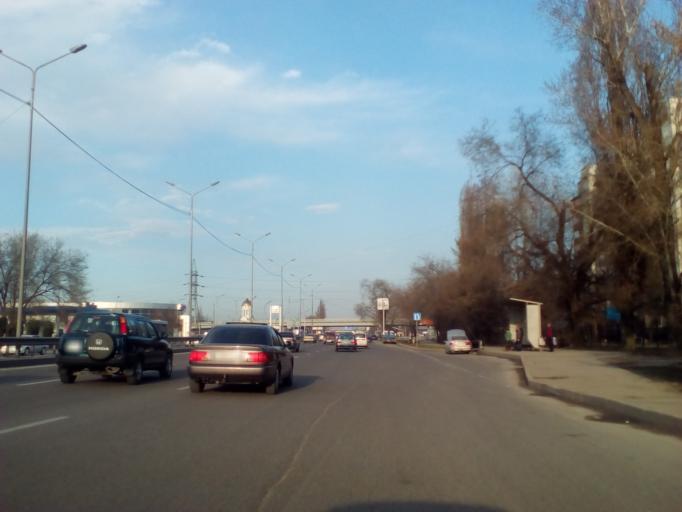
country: KZ
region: Almaty Qalasy
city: Almaty
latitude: 43.2422
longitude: 76.8237
